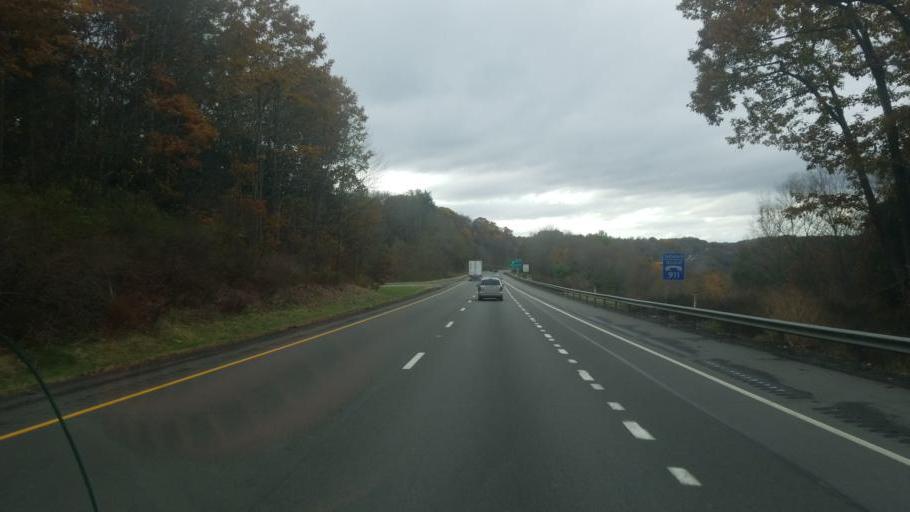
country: US
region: Pennsylvania
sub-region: Clarion County
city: Clarion
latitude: 41.1864
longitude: -79.4033
